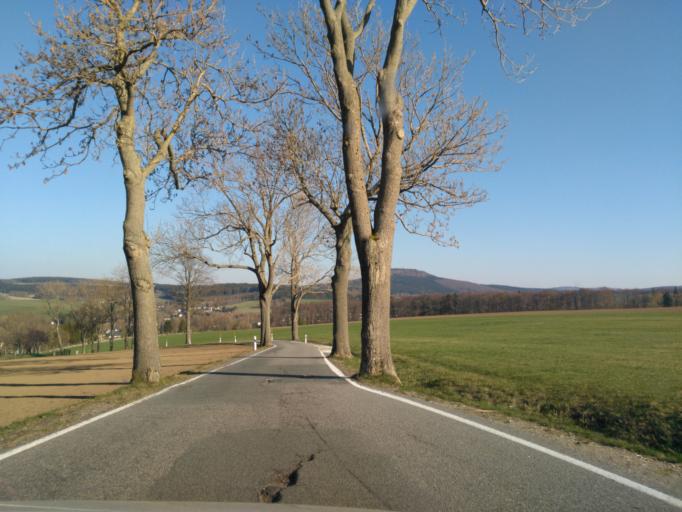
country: DE
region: Saxony
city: Schlettau
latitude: 50.5390
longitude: 12.9811
